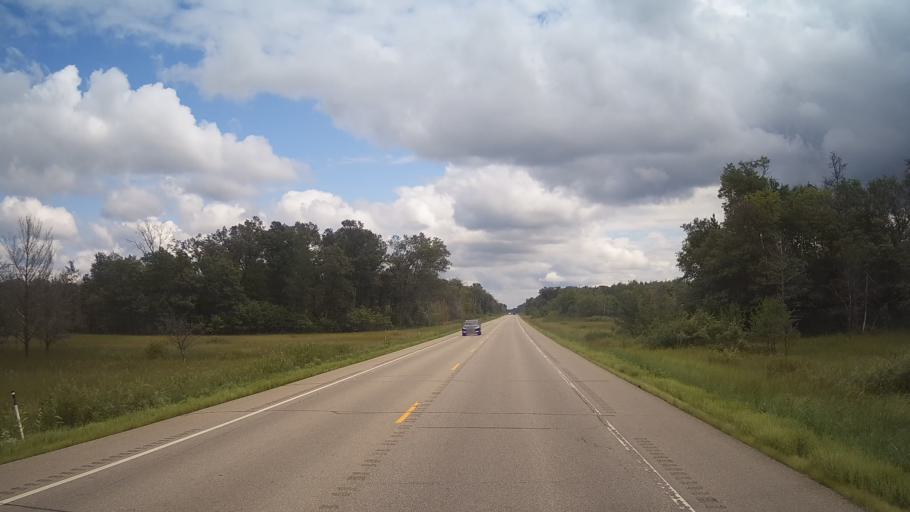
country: US
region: Wisconsin
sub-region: Adams County
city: Friendship
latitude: 44.0252
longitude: -89.7391
